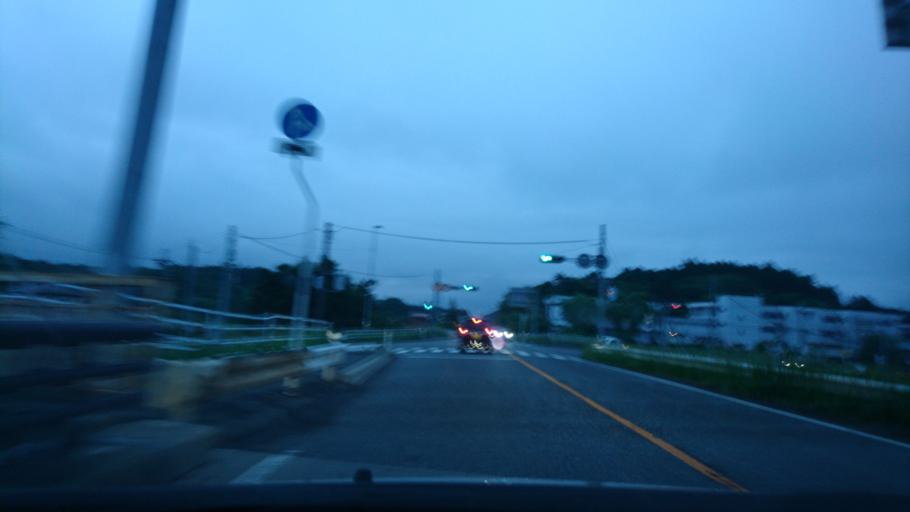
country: JP
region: Iwate
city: Ichinoseki
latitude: 38.7977
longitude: 141.0546
